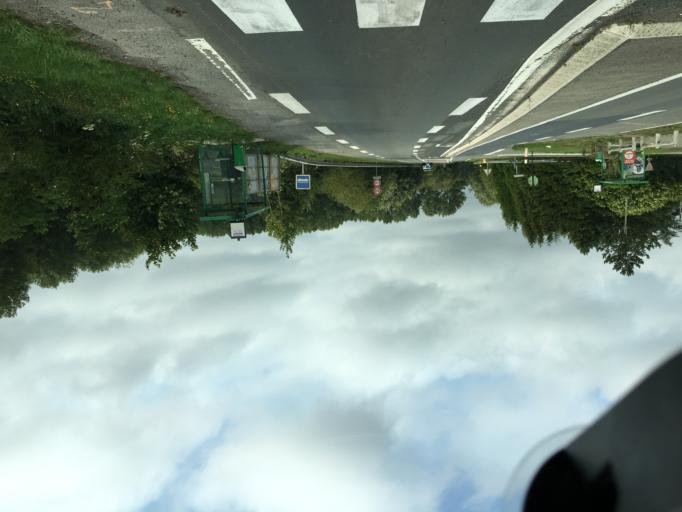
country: FR
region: Nord-Pas-de-Calais
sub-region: Departement du Pas-de-Calais
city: Camblain-Chatelain
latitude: 50.4341
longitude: 2.4514
